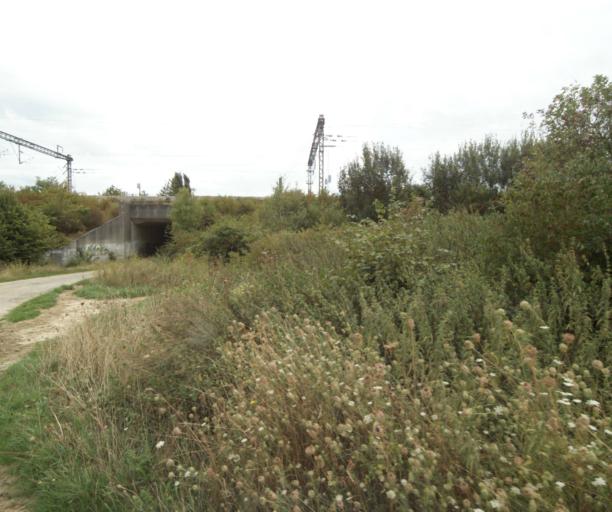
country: FR
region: Nord-Pas-de-Calais
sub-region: Departement du Nord
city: Sainghin-en-Melantois
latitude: 50.5716
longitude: 3.1638
